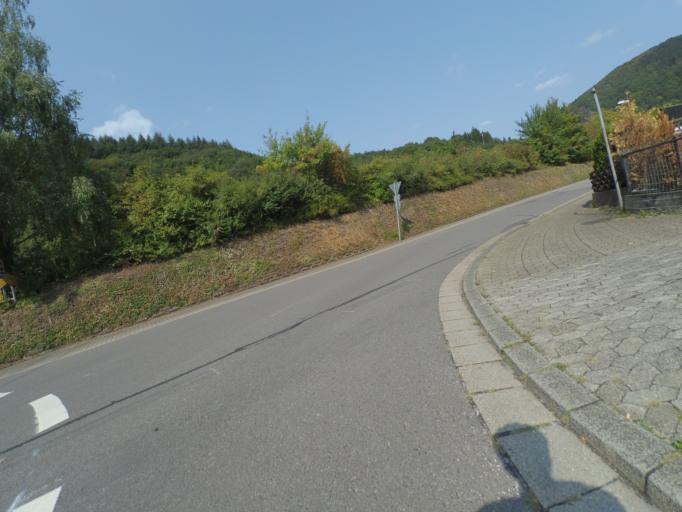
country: DE
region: Saarland
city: Saarhoelzbach
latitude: 49.5156
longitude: 6.6044
